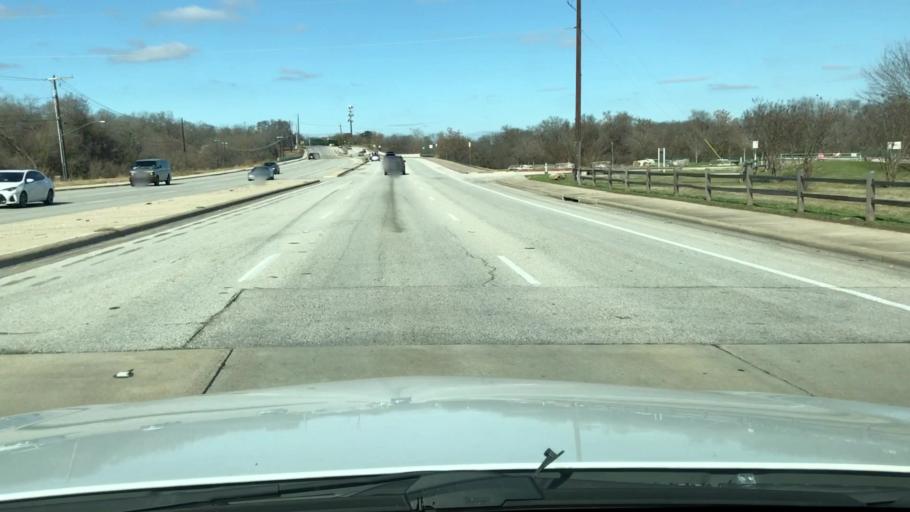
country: US
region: Texas
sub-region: Travis County
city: Onion Creek
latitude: 30.1757
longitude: -97.7435
